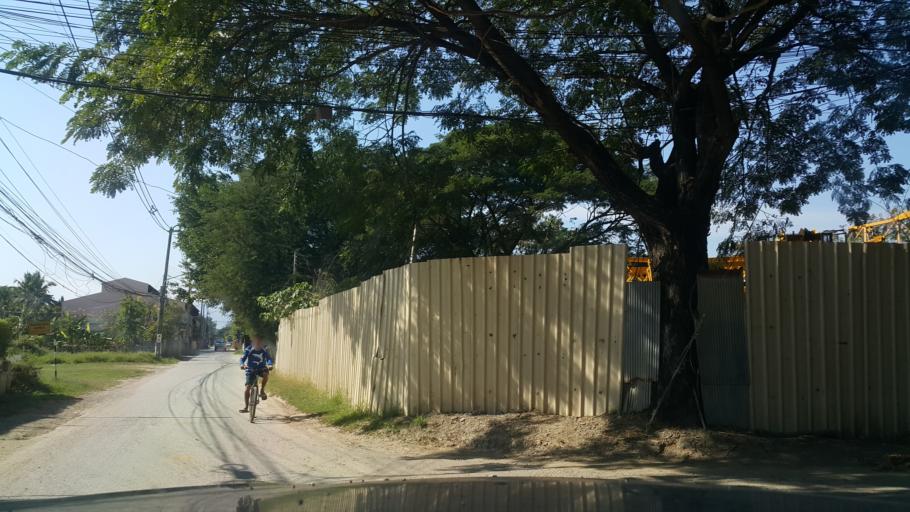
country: TH
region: Chiang Mai
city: Chiang Mai
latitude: 18.7736
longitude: 99.0339
